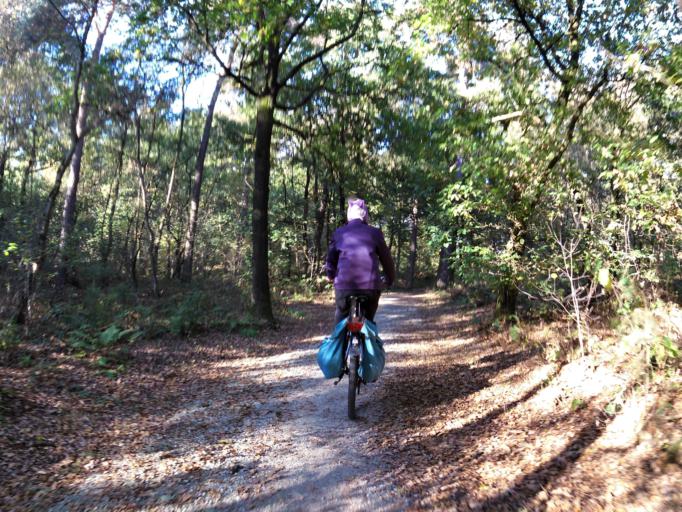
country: NL
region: Limburg
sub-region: Gemeente Bergen
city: Wellerlooi
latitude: 51.5268
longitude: 6.1488
